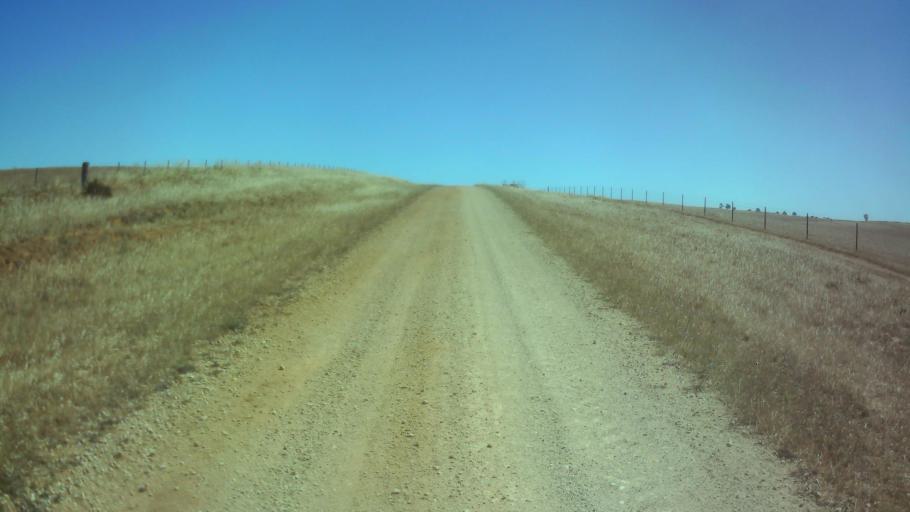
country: AU
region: New South Wales
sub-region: Weddin
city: Grenfell
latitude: -33.9754
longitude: 148.3602
